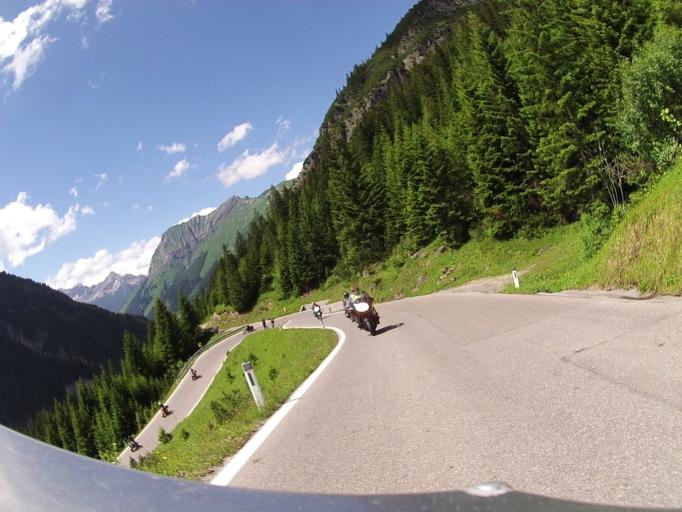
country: AT
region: Tyrol
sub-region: Politischer Bezirk Reutte
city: Gramais
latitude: 47.2854
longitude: 10.6114
